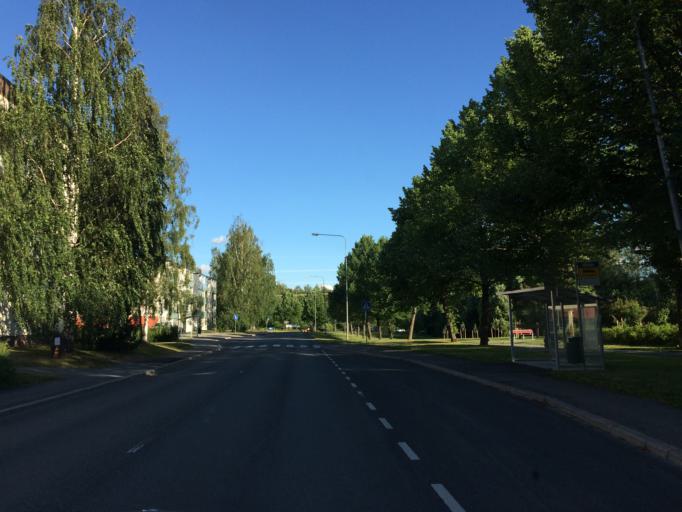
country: FI
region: Haeme
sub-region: Haemeenlinna
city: Haemeenlinna
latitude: 61.0027
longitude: 24.4972
